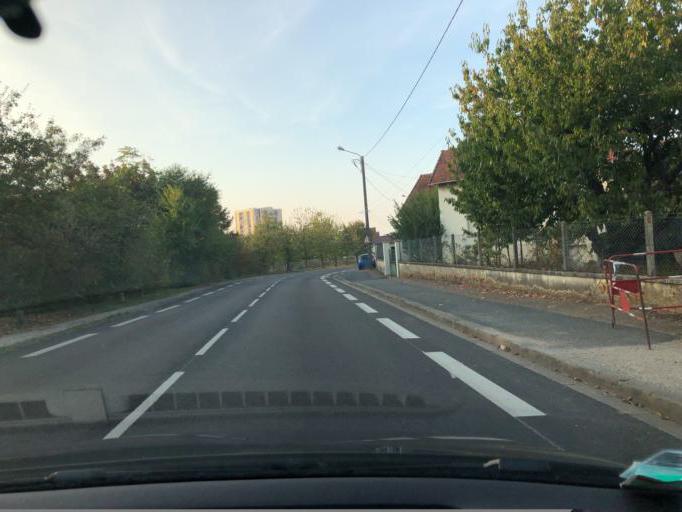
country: FR
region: Bourgogne
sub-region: Departement de l'Yonne
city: Sens
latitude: 48.2023
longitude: 3.2979
